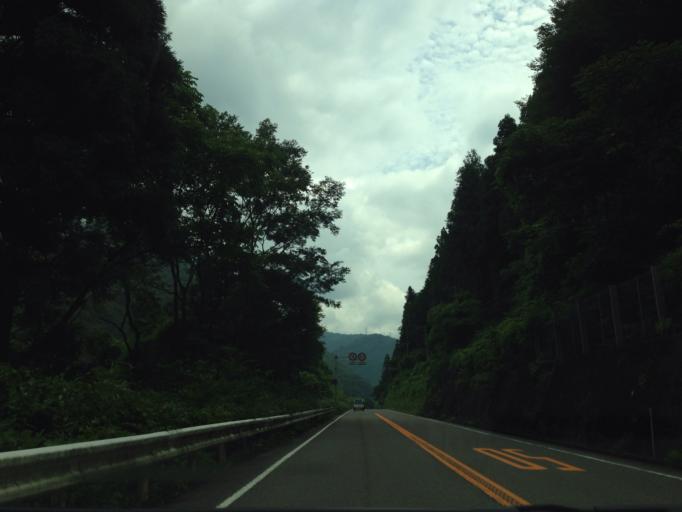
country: JP
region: Gifu
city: Mitake
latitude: 35.5413
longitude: 137.1415
